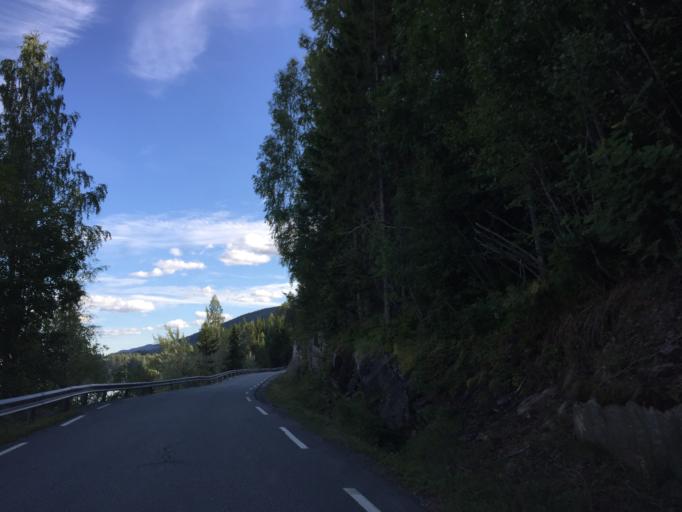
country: NO
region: Buskerud
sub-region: Ovre Eiker
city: Hokksund
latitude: 59.6536
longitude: 9.9141
